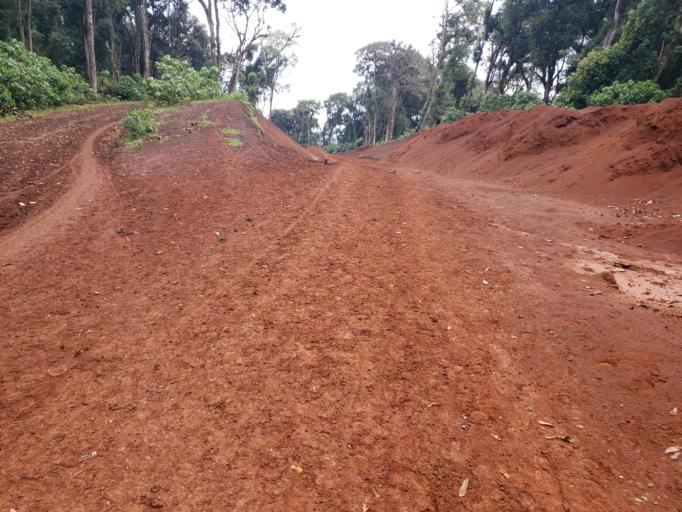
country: ET
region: Oromiya
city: Dodola
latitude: 6.5939
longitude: 39.4126
